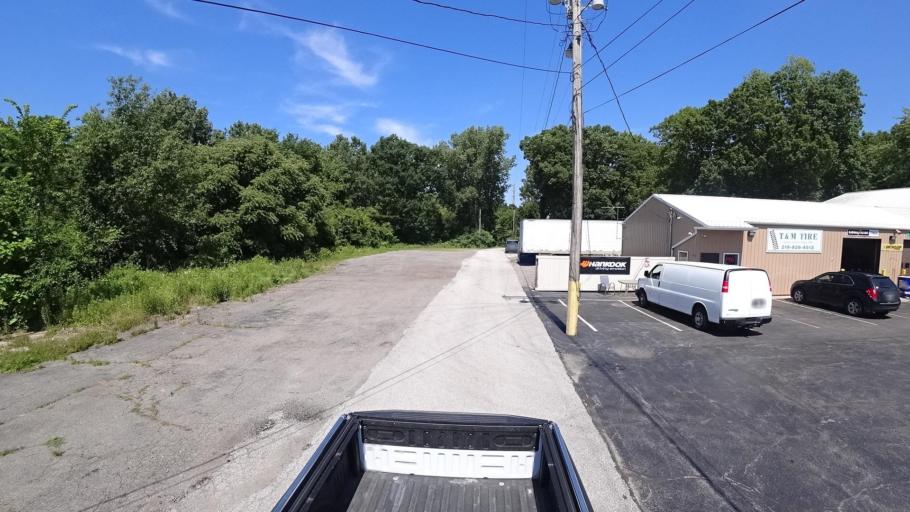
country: US
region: Indiana
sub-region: Porter County
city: Porter
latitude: 41.6142
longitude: -87.0957
